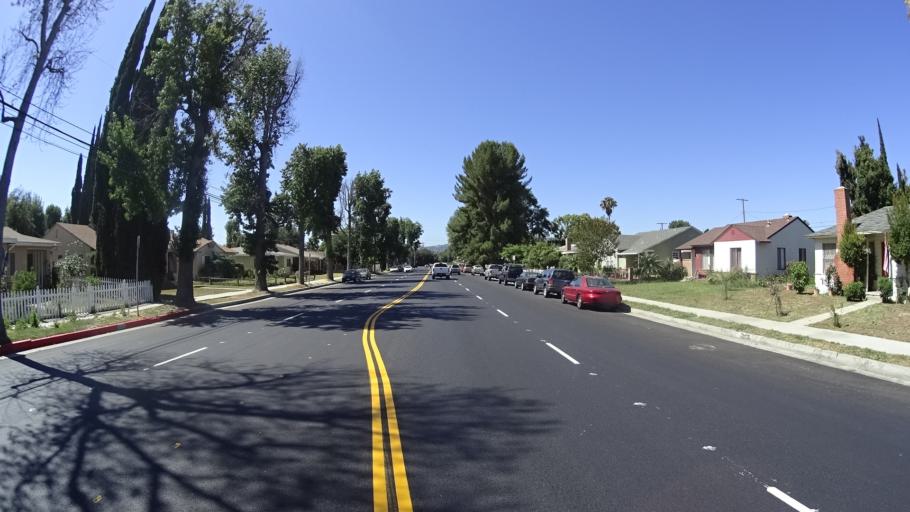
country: US
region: California
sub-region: Los Angeles County
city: Van Nuys
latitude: 34.1891
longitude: -118.4924
